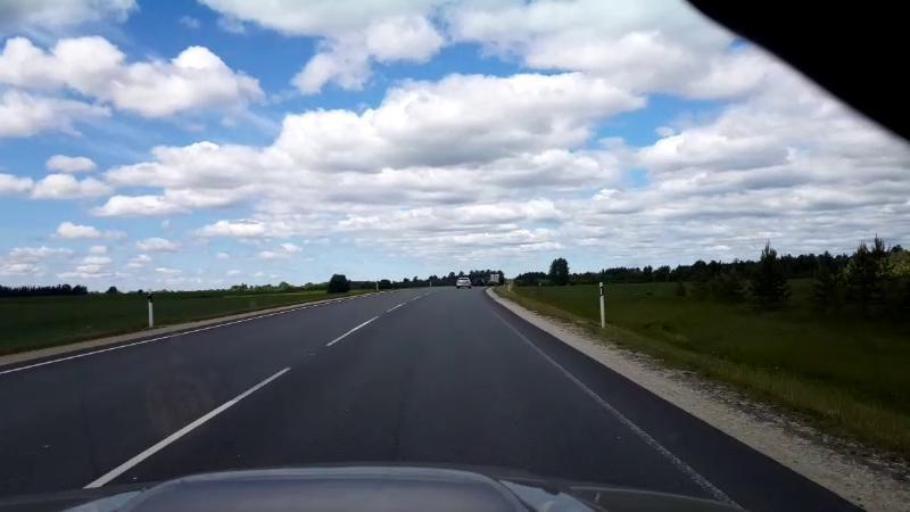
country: EE
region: Paernumaa
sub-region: Halinga vald
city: Parnu-Jaagupi
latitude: 58.6926
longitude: 24.4330
